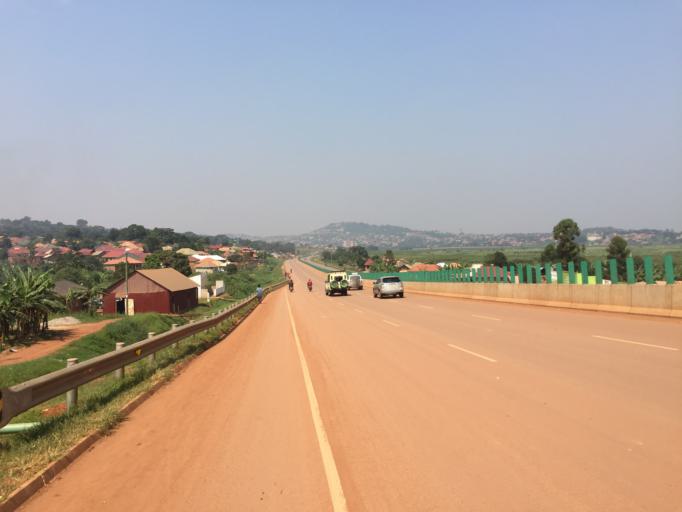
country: UG
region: Central Region
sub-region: Wakiso District
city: Kajansi
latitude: 0.2220
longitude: 32.6049
